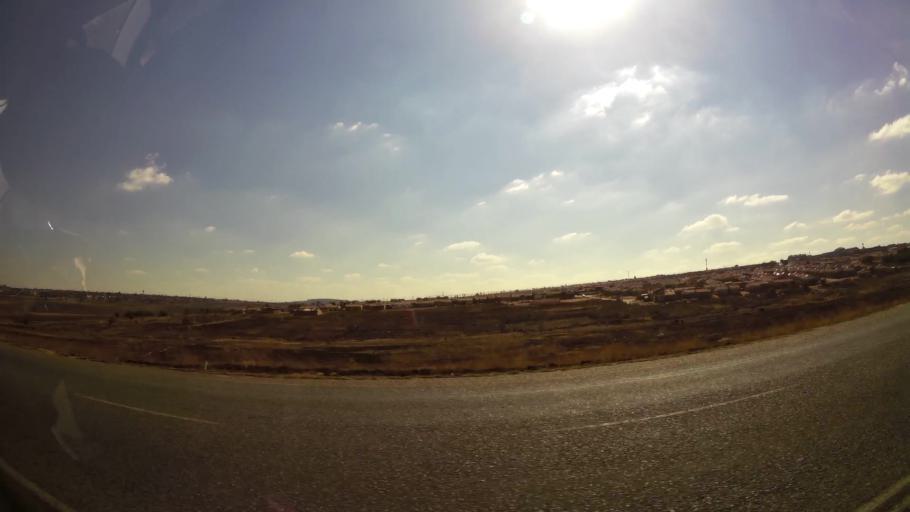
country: ZA
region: Gauteng
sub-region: West Rand District Municipality
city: Randfontein
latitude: -26.1747
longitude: 27.7760
